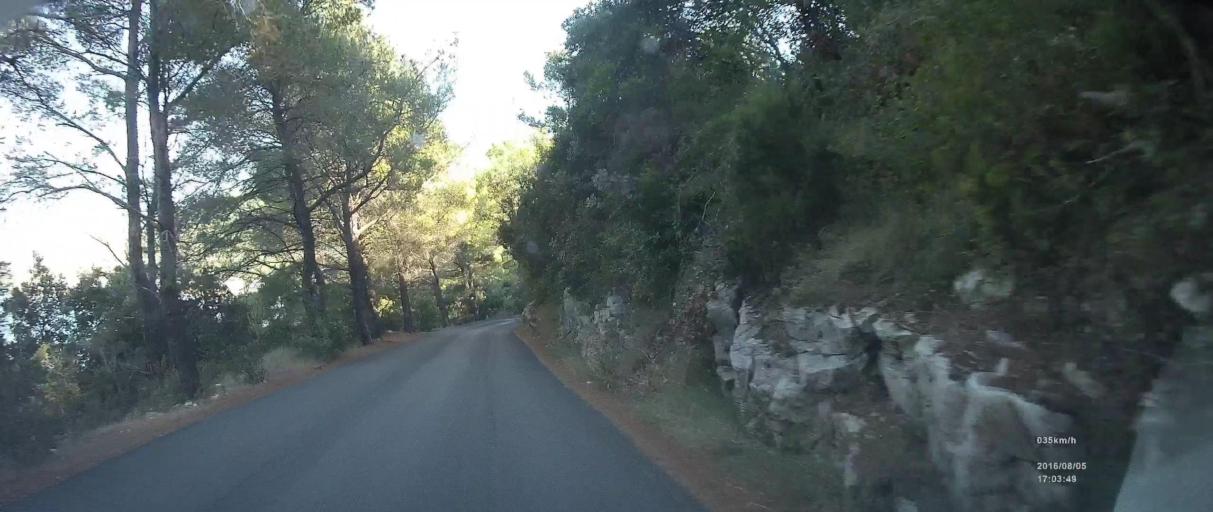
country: HR
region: Dubrovacko-Neretvanska
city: Blato
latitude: 42.7888
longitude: 17.3741
